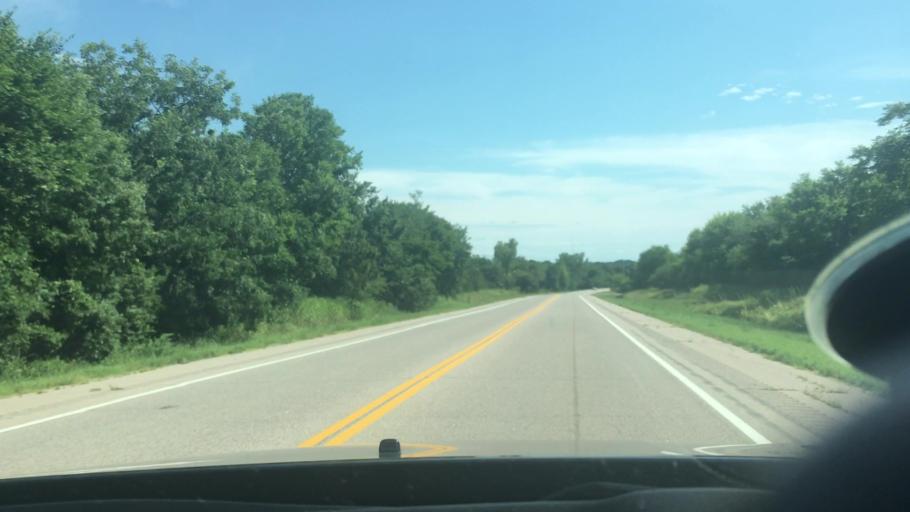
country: US
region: Oklahoma
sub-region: Seminole County
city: Konawa
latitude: 34.9590
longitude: -96.6787
